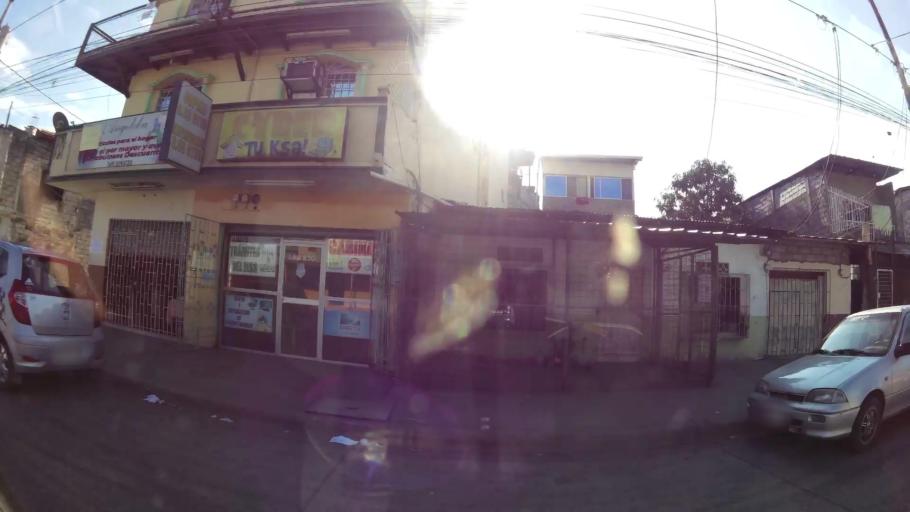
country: EC
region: Guayas
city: Guayaquil
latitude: -2.2274
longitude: -79.9300
